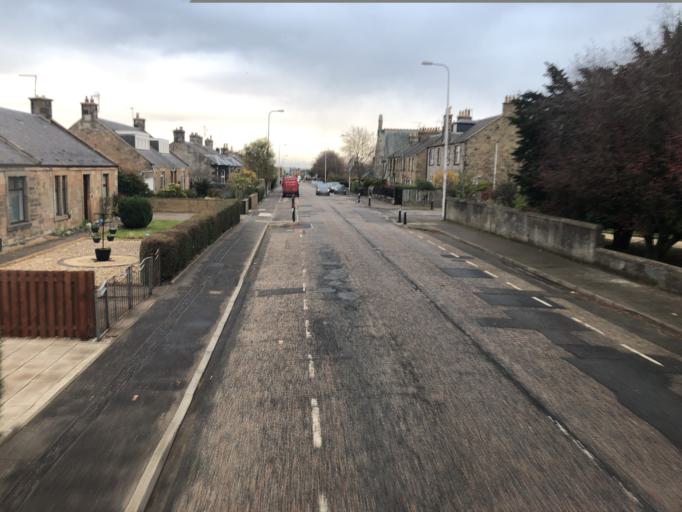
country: GB
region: Scotland
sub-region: Midlothian
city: Loanhead
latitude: 55.8764
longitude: -3.1578
